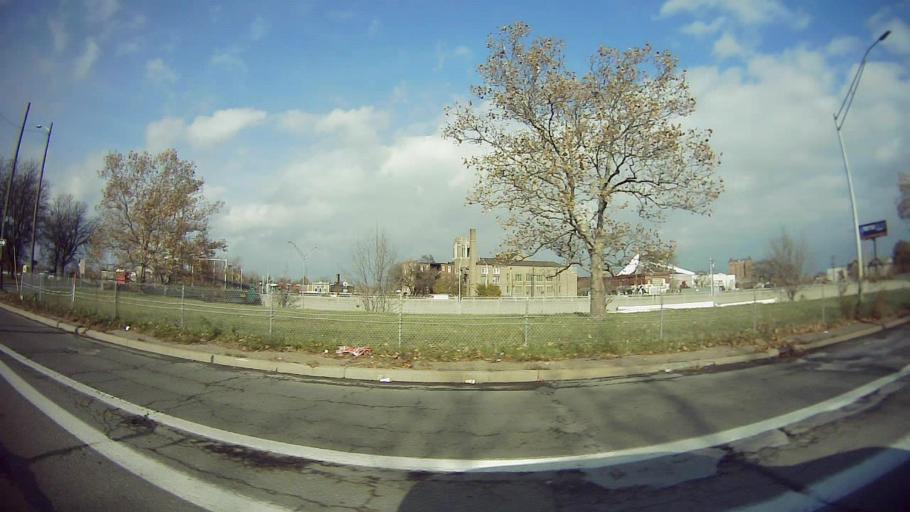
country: US
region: Michigan
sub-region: Wayne County
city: Highland Park
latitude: 42.3534
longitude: -83.1102
